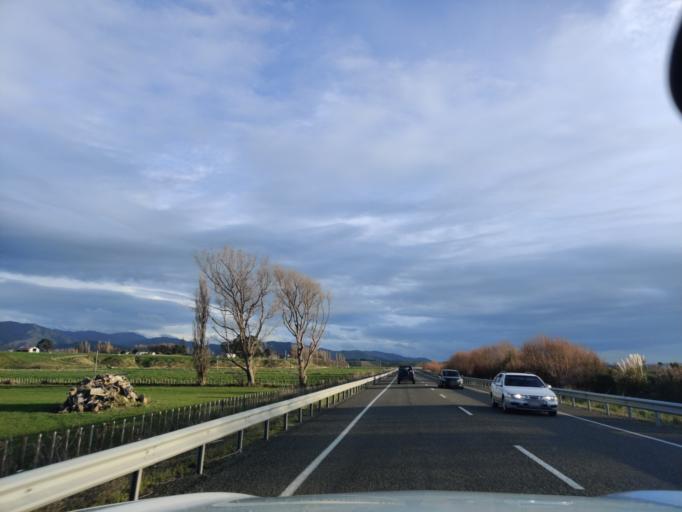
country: NZ
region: Manawatu-Wanganui
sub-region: Horowhenua District
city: Foxton
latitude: -40.5226
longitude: 175.4444
